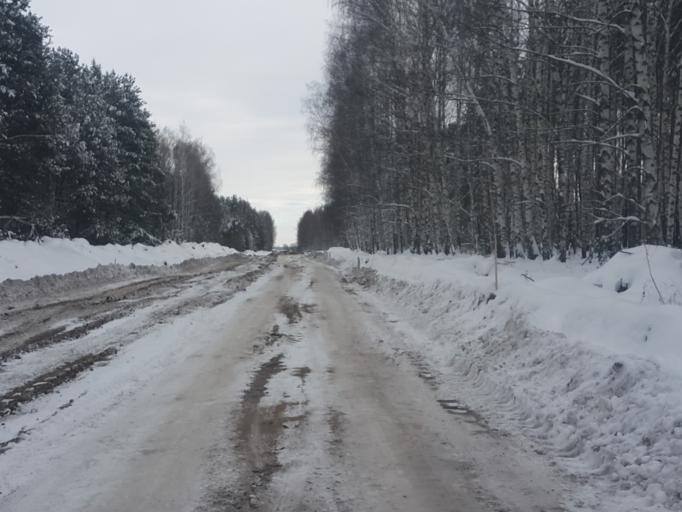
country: RU
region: Tambov
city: Platonovka
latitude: 52.8849
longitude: 41.8602
